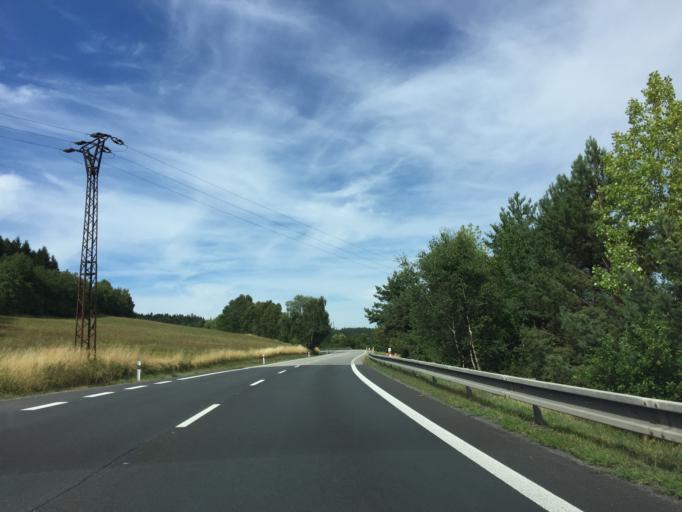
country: CZ
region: Central Bohemia
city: Votice
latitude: 49.5762
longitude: 14.6616
